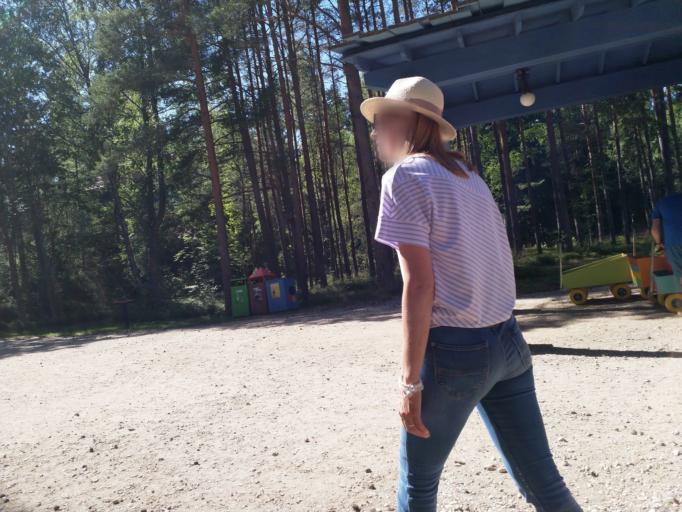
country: EE
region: Paernumaa
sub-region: Paikuse vald
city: Paikuse
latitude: 58.3037
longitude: 24.5906
